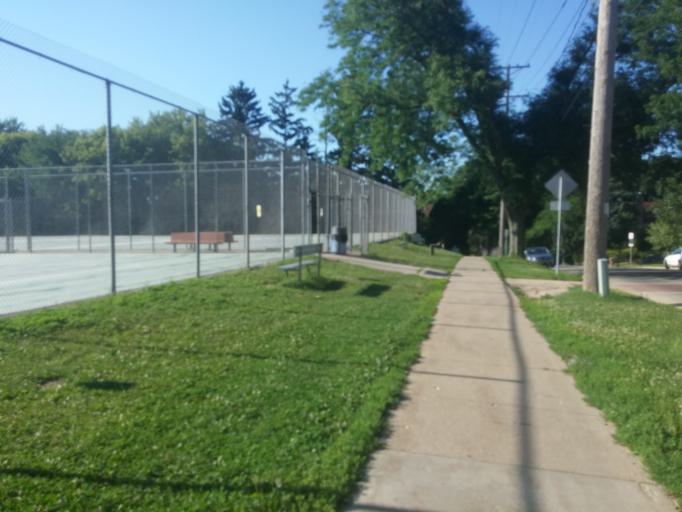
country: US
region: Wisconsin
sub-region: Dane County
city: Shorewood Hills
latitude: 43.0688
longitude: -89.4288
